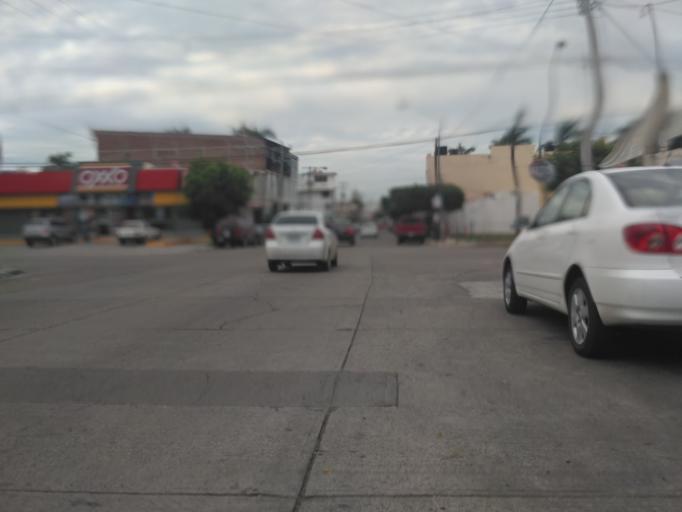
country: MX
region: Sinaloa
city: Culiacan
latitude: 24.8006
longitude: -107.3976
